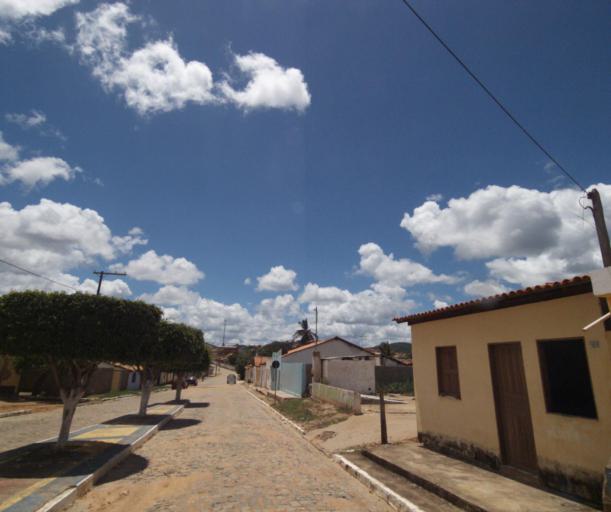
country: BR
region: Bahia
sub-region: Pocoes
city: Pocoes
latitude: -14.3752
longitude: -40.5014
